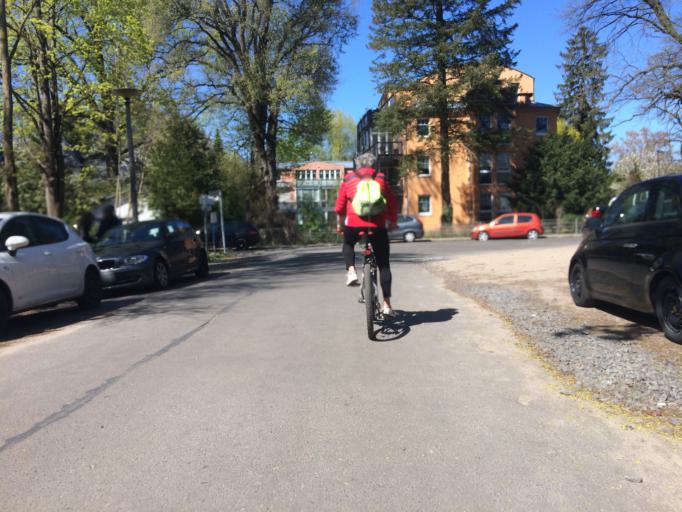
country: DE
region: Berlin
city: Rahnsdorf
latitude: 52.4388
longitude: 13.6841
